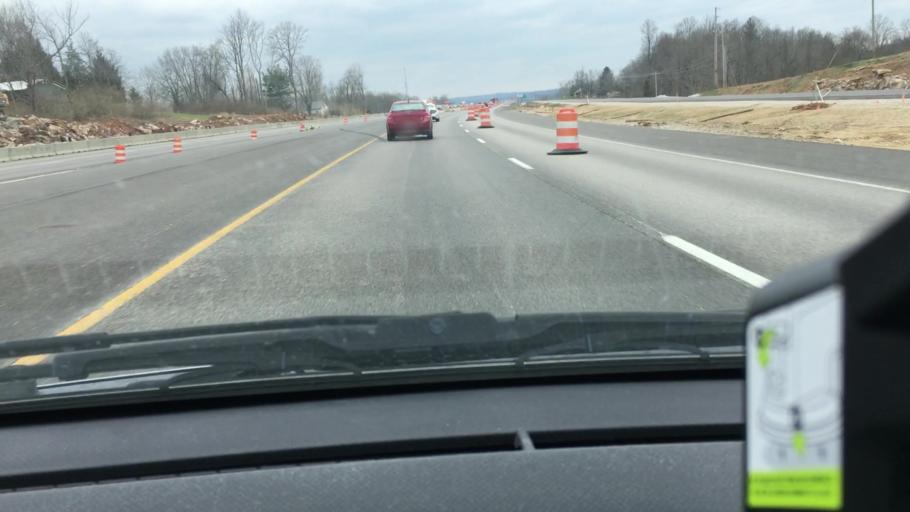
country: US
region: Indiana
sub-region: Monroe County
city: Bloomington
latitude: 39.2596
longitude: -86.5242
